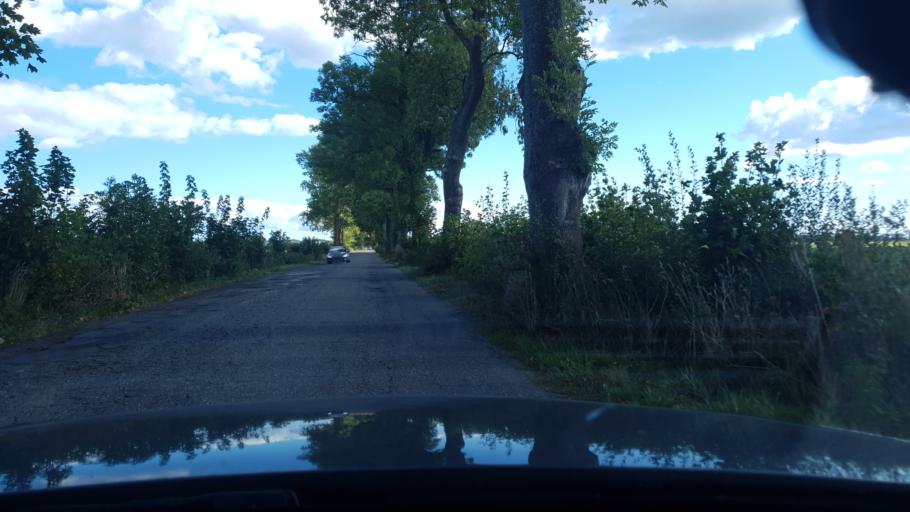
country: PL
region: Pomeranian Voivodeship
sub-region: Powiat pucki
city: Zelistrzewo
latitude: 54.6878
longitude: 18.4356
